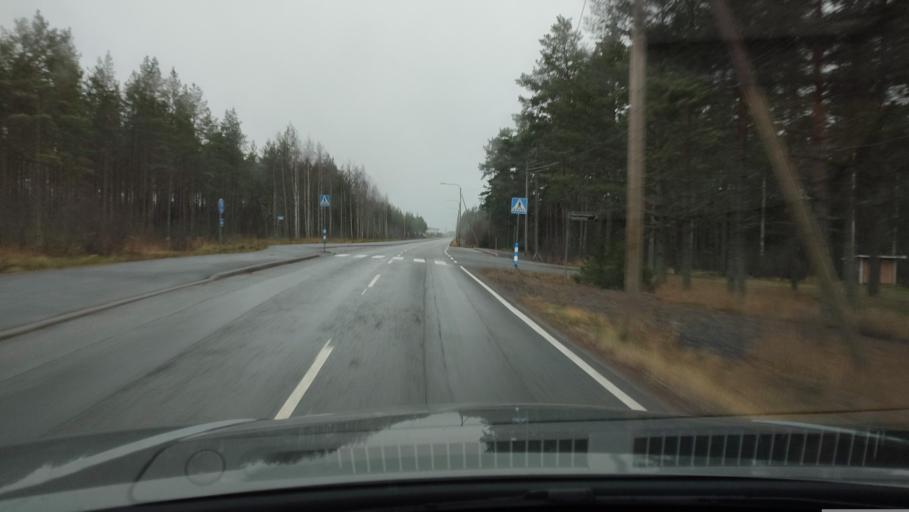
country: FI
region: Ostrobothnia
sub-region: Sydosterbotten
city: Kristinestad
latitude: 62.2360
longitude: 21.5208
